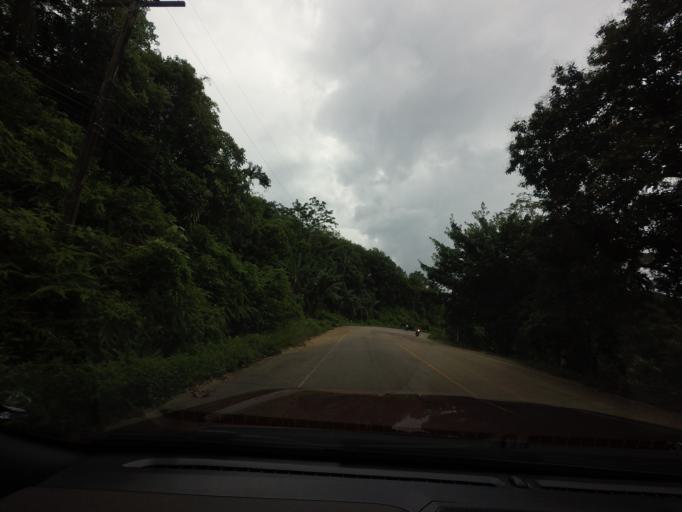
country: TH
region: Narathiwat
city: Sukhirin
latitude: 5.9859
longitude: 101.6862
